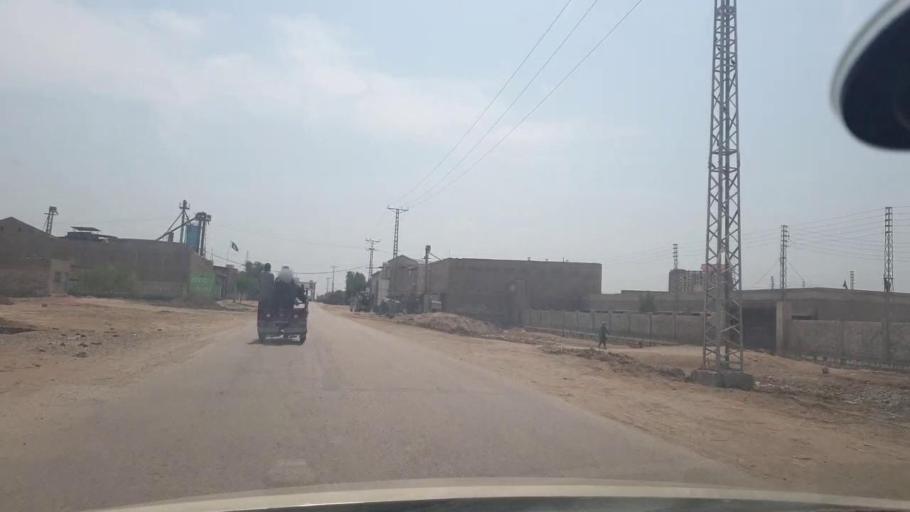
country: PK
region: Sindh
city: Jacobabad
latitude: 28.2455
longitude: 68.4661
